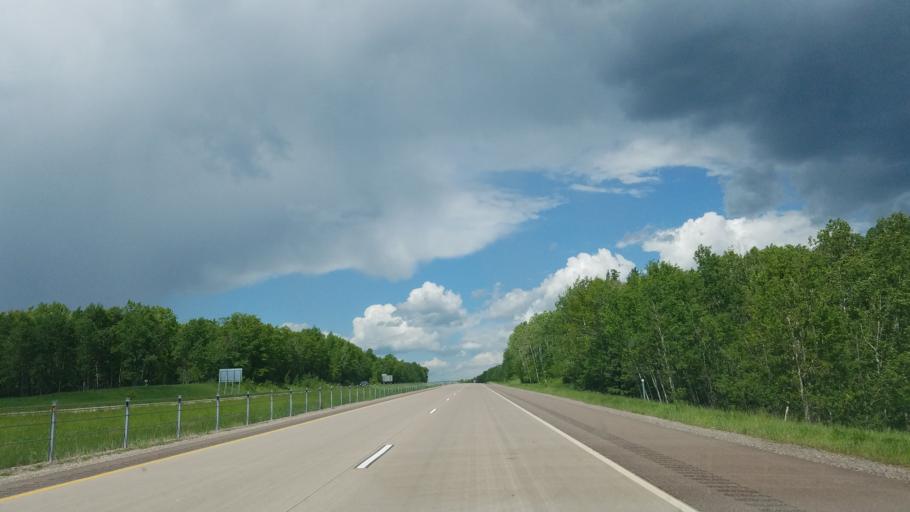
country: US
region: Minnesota
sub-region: Carlton County
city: Moose Lake
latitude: 46.4592
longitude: -92.7249
